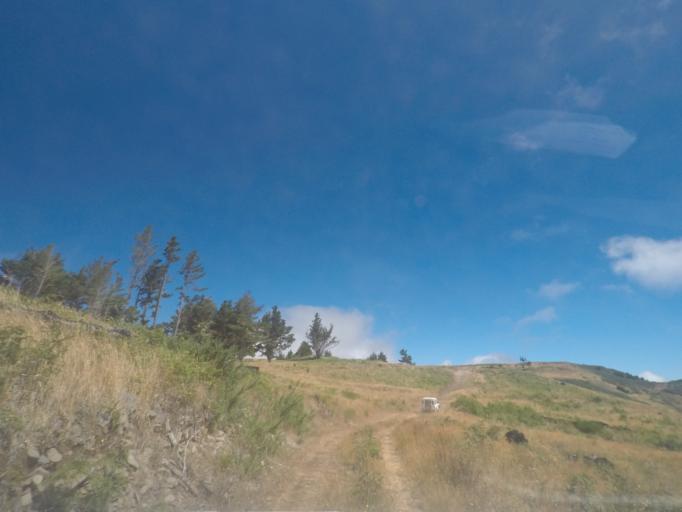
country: PT
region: Madeira
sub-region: Funchal
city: Nossa Senhora do Monte
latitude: 32.7106
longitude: -16.9063
